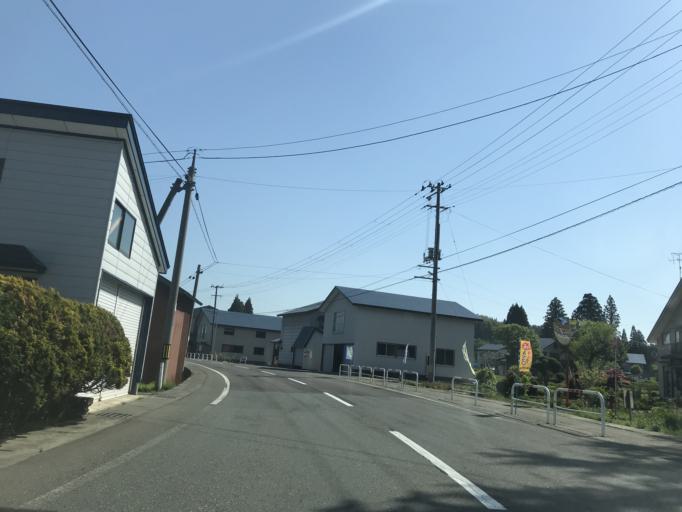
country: JP
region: Akita
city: Yokotemachi
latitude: 39.4229
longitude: 140.7452
